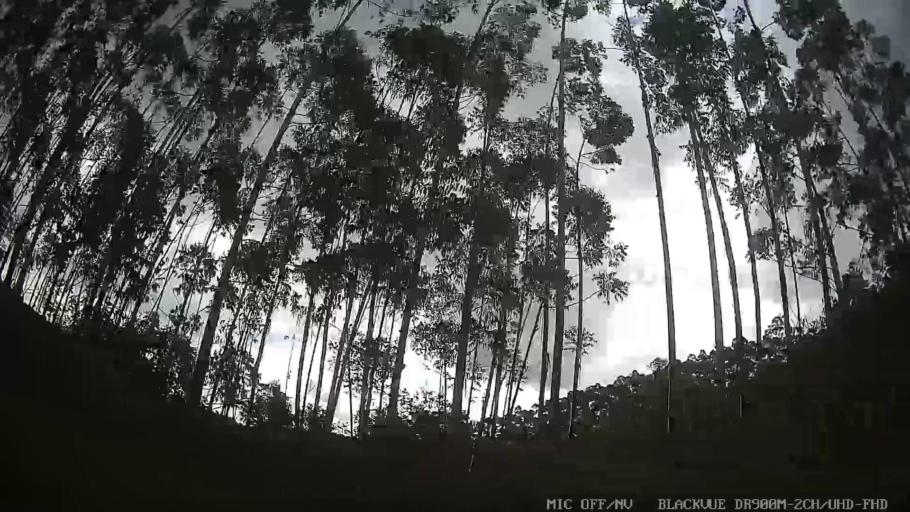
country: BR
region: Sao Paulo
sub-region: Santa Branca
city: Santa Branca
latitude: -23.5545
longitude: -45.6737
